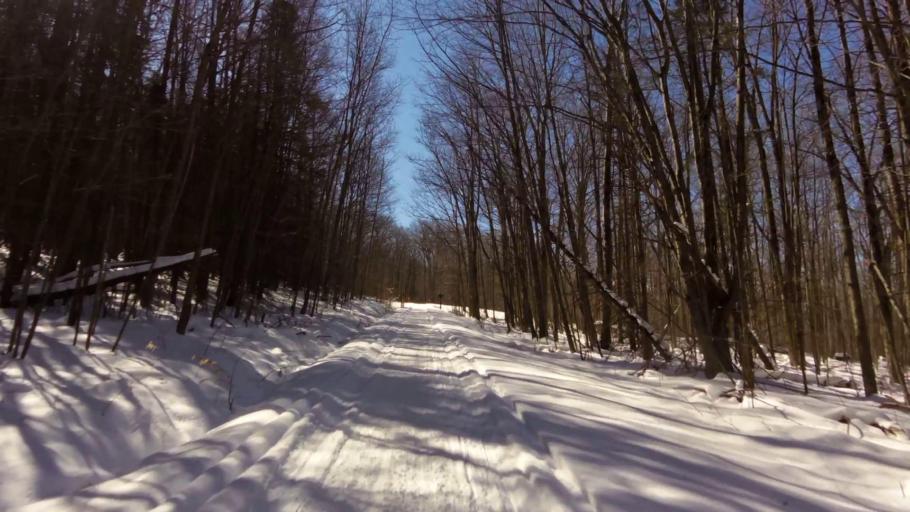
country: US
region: New York
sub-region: Allegany County
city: Houghton
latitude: 42.3572
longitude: -78.1935
